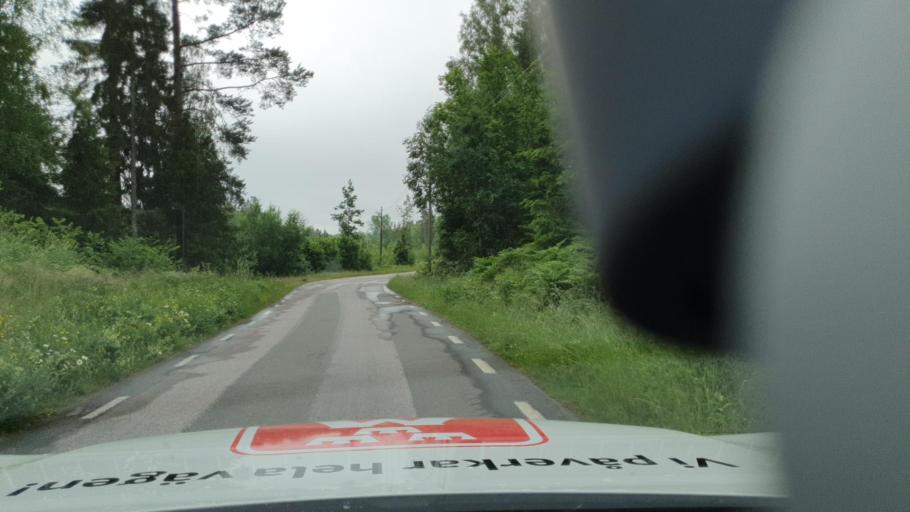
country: SE
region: Vaestra Goetaland
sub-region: Gullspangs Kommun
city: Gullspang
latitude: 59.0404
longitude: 14.1542
